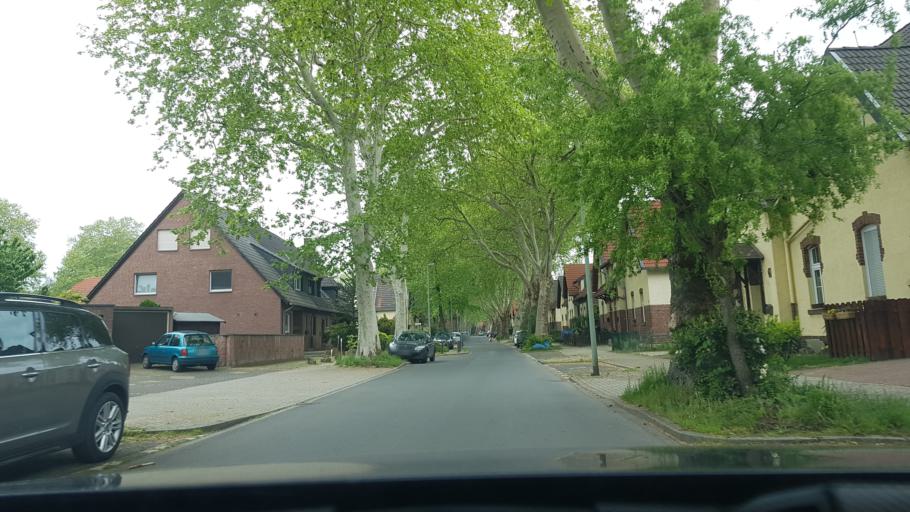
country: DE
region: North Rhine-Westphalia
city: Meiderich
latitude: 51.5018
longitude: 6.8084
